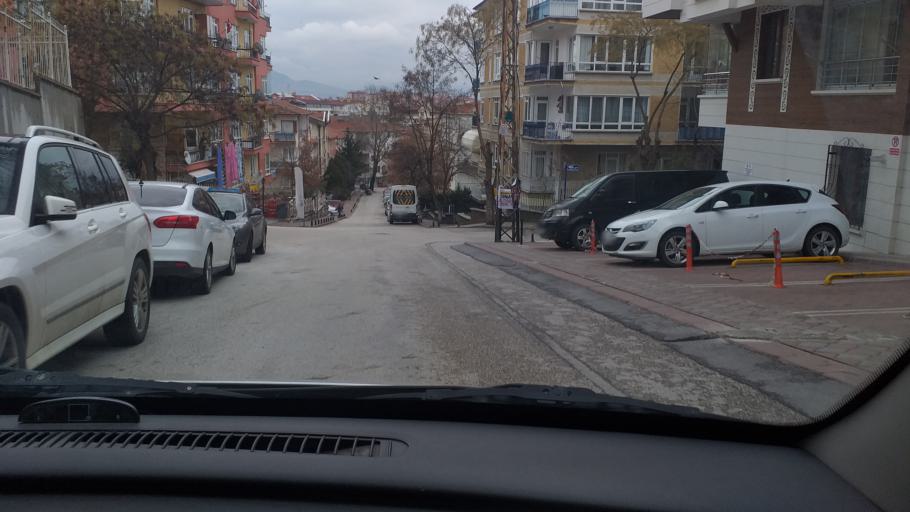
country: TR
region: Ankara
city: Ankara
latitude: 39.9777
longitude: 32.8375
